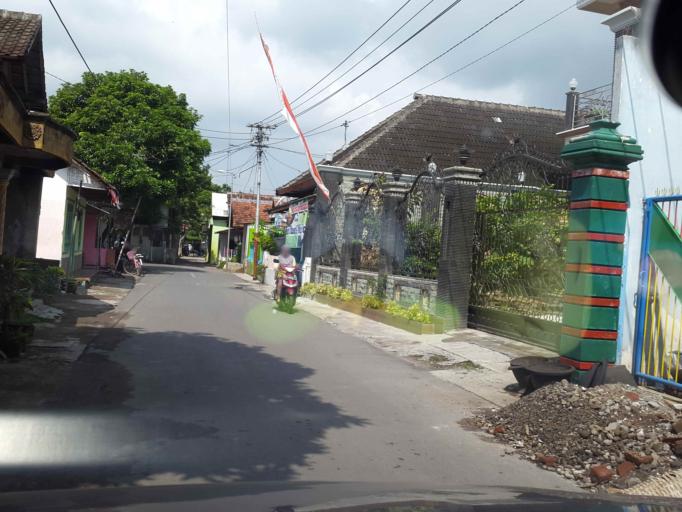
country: ID
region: East Java
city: Blitar
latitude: -8.0999
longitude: 112.1528
